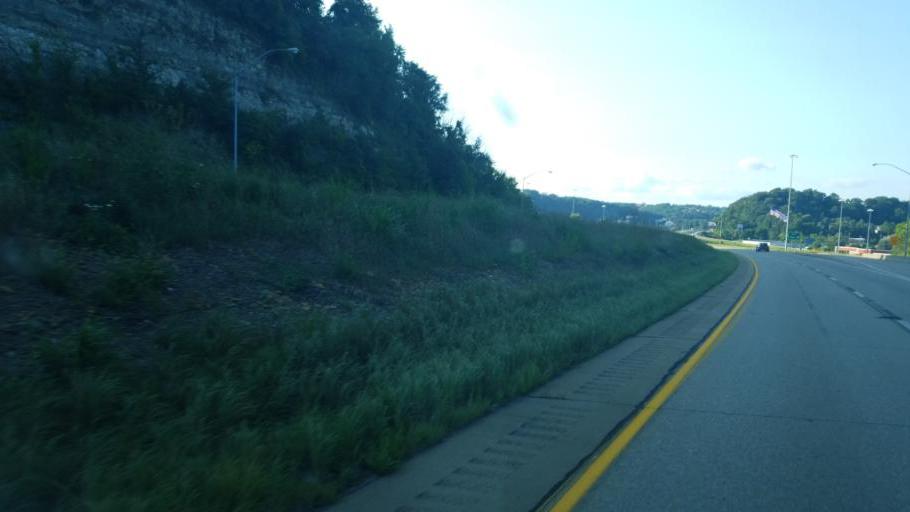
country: US
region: Pennsylvania
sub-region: Allegheny County
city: Bridgeville
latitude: 40.3506
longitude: -80.1172
